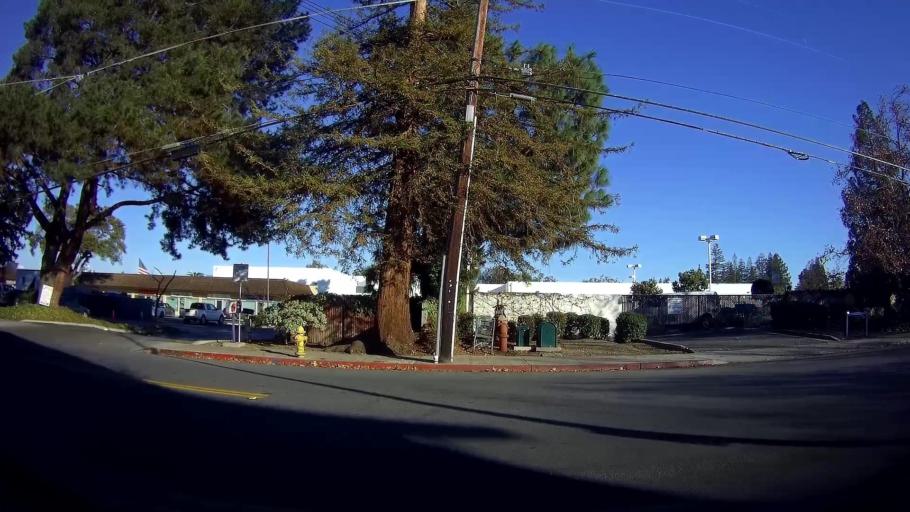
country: US
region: California
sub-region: Santa Clara County
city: Santa Clara
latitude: 37.3221
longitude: -121.9663
